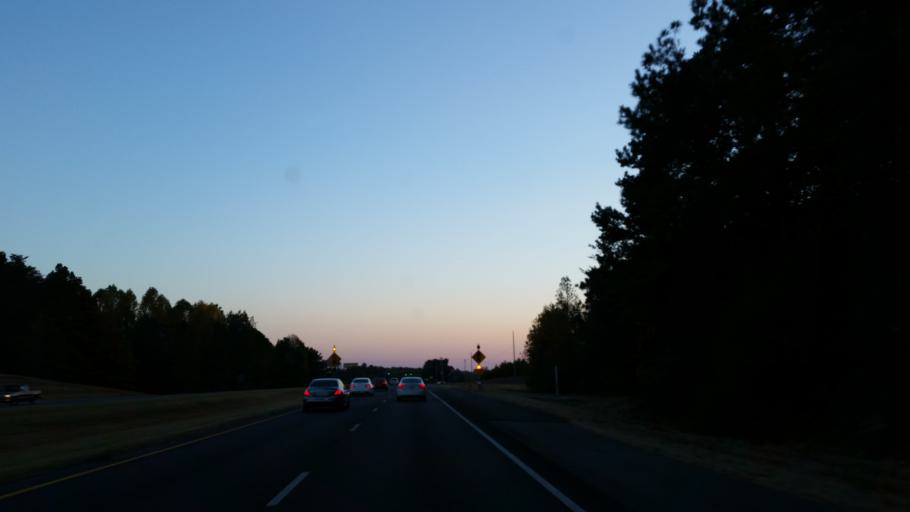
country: US
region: Georgia
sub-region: Dawson County
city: Dawsonville
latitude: 34.3155
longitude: -84.0640
